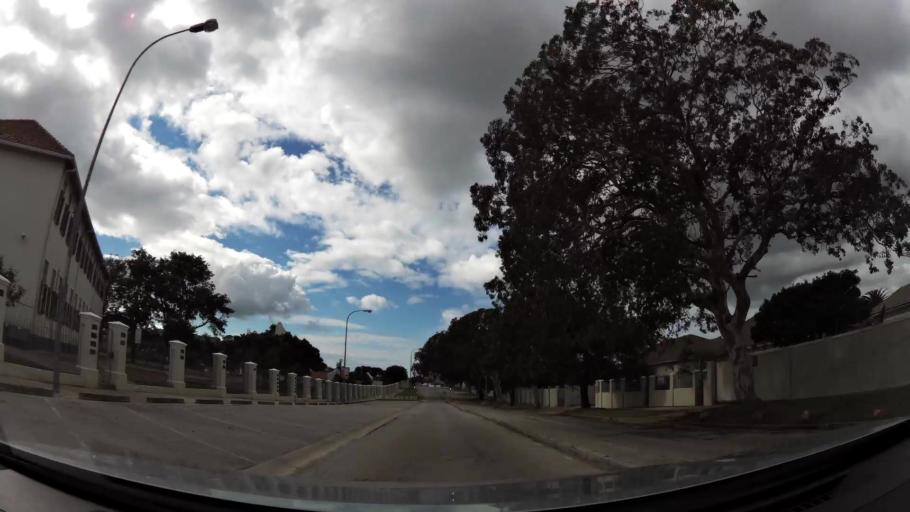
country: ZA
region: Eastern Cape
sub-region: Nelson Mandela Bay Metropolitan Municipality
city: Port Elizabeth
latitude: -33.9621
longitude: 25.5973
